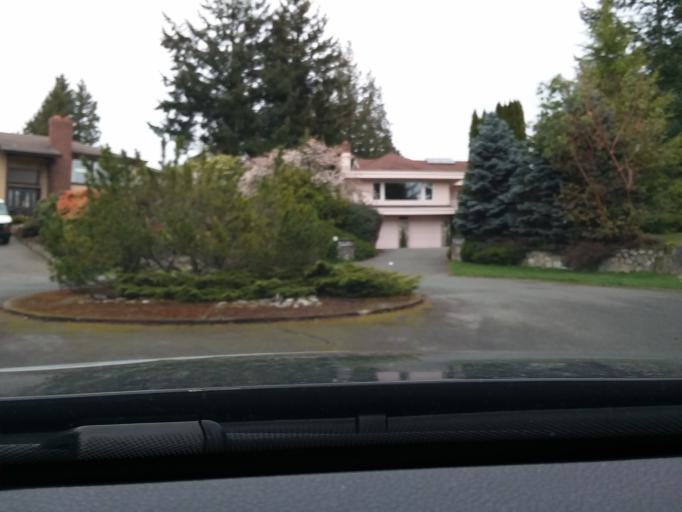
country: CA
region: British Columbia
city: North Saanich
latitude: 48.6154
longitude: -123.4263
